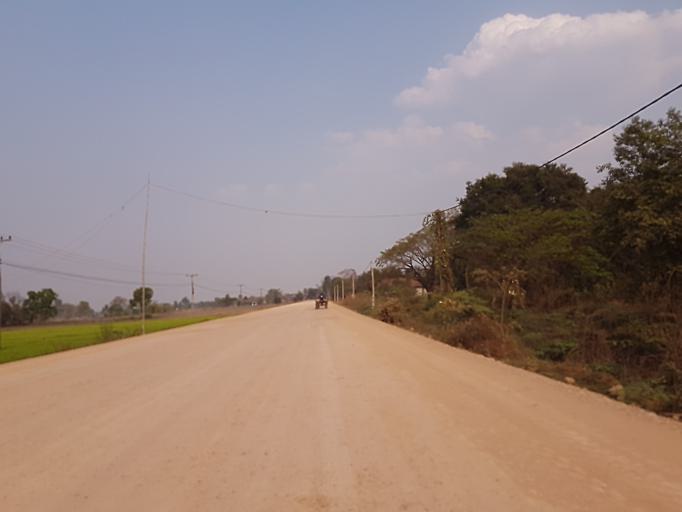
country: TH
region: Nong Khai
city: Nong Khai
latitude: 17.9812
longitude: 102.8818
